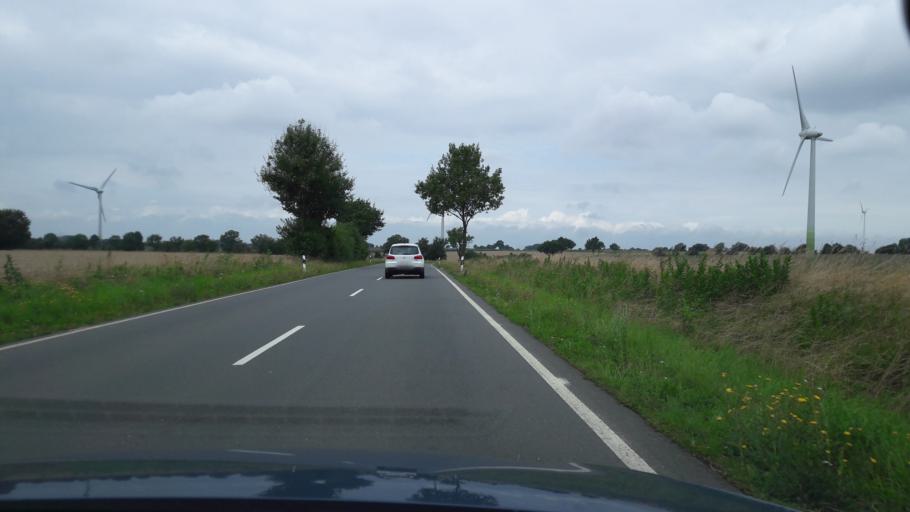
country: DE
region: North Rhine-Westphalia
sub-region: Regierungsbezirk Munster
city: Ennigerloh
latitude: 51.8579
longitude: 7.9792
